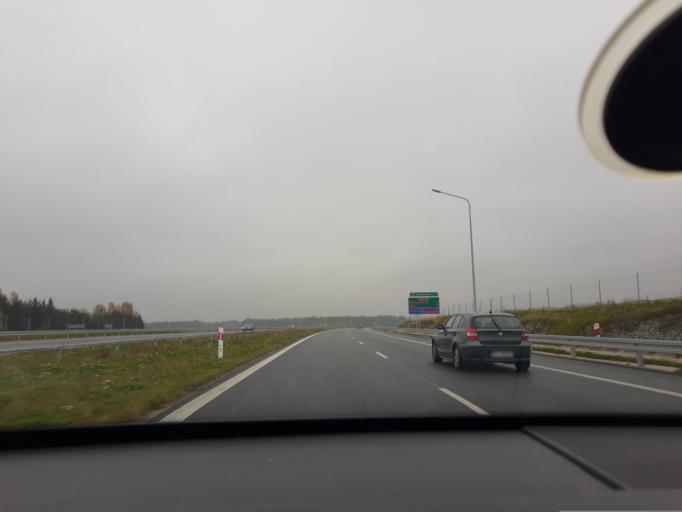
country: PL
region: Lodz Voivodeship
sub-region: Powiat pabianicki
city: Pabianice
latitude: 51.7056
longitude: 19.3419
